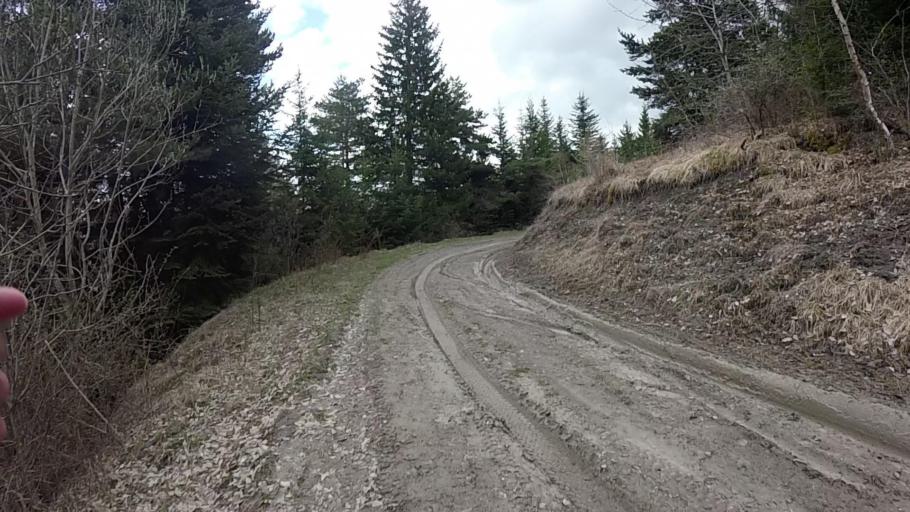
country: FR
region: Provence-Alpes-Cote d'Azur
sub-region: Departement des Alpes-de-Haute-Provence
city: Seyne-les-Alpes
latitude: 44.3294
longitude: 6.3307
